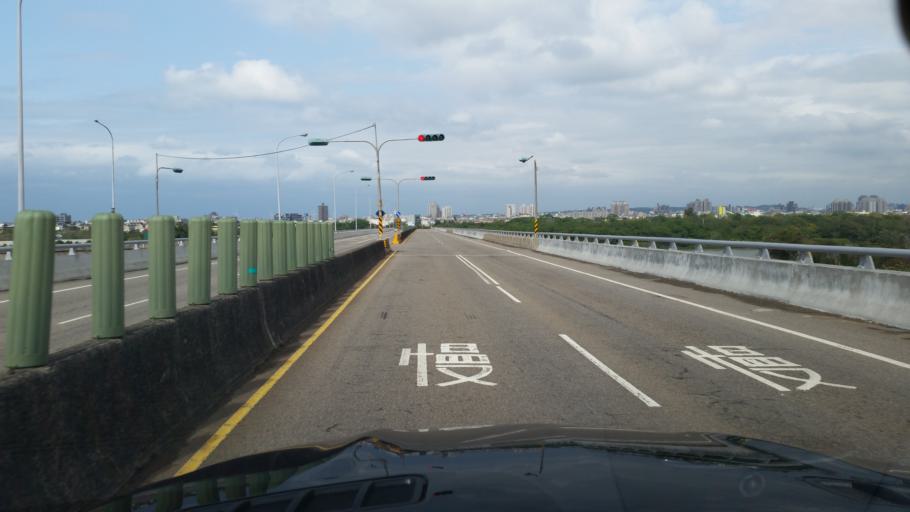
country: TW
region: Taiwan
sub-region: Miaoli
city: Miaoli
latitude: 24.6634
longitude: 120.8669
